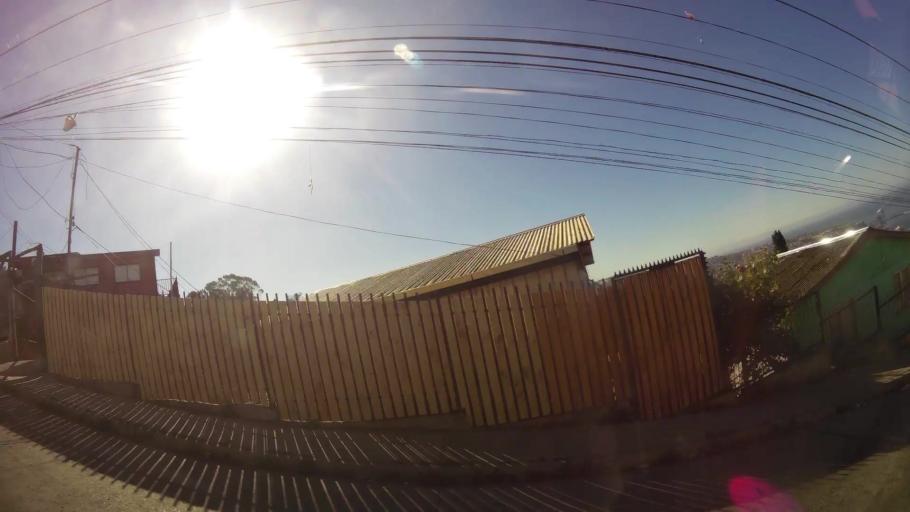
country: CL
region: Valparaiso
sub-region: Provincia de Valparaiso
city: Valparaiso
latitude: -33.0574
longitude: -71.6216
